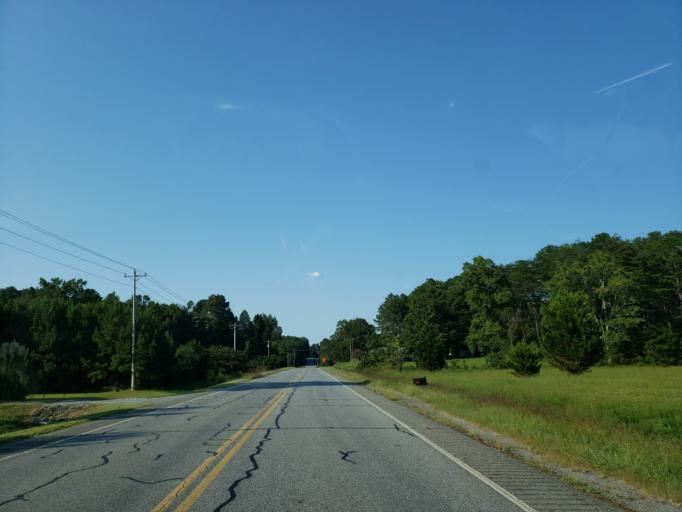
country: US
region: Tennessee
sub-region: Bradley County
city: Wildwood Lake
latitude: 34.9690
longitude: -84.7326
